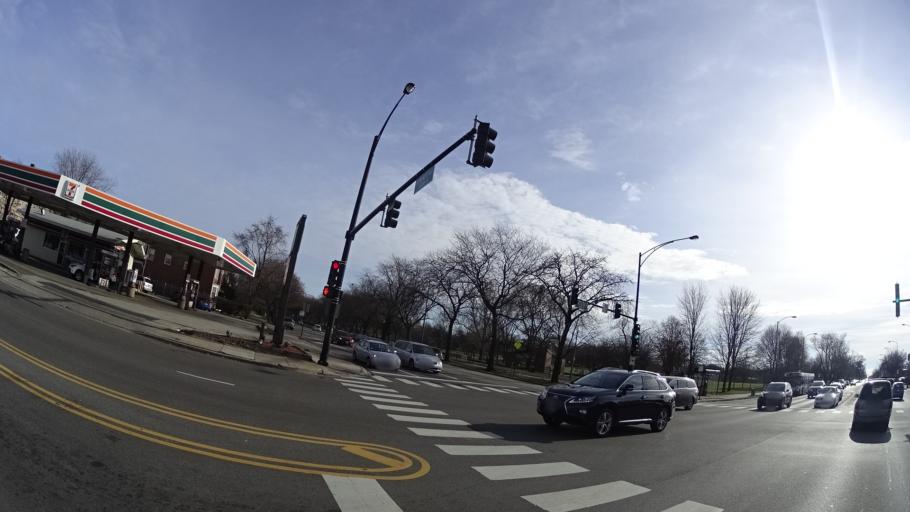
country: US
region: Illinois
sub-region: Cook County
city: Evanston
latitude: 42.0052
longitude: -87.6901
